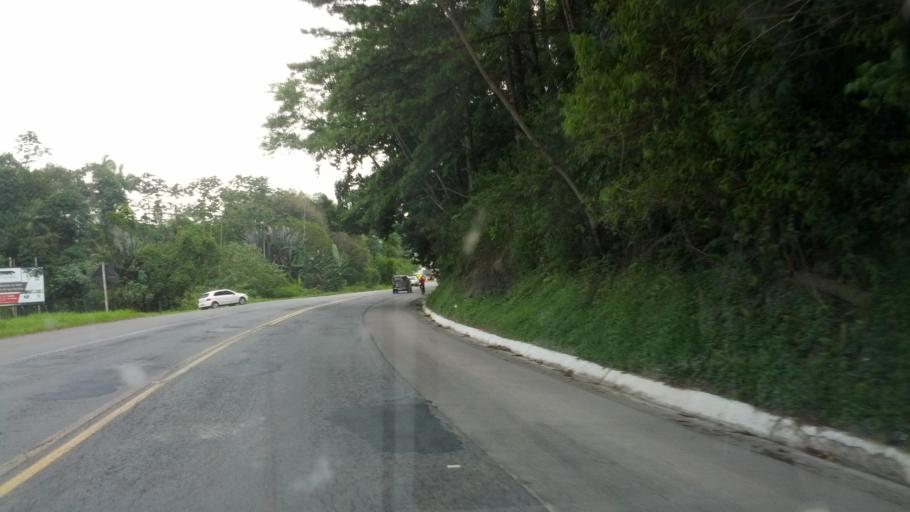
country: BR
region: Santa Catarina
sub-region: Blumenau
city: Blumenau
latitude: -26.8711
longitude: -49.1079
